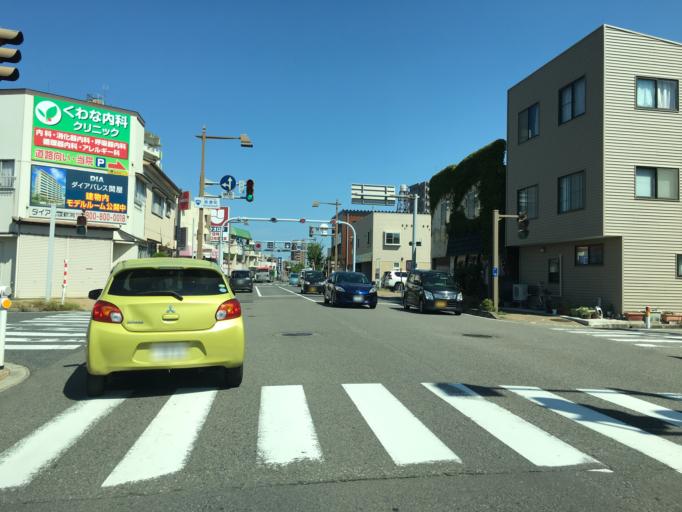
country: JP
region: Niigata
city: Niigata-shi
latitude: 37.9053
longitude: 139.0120
